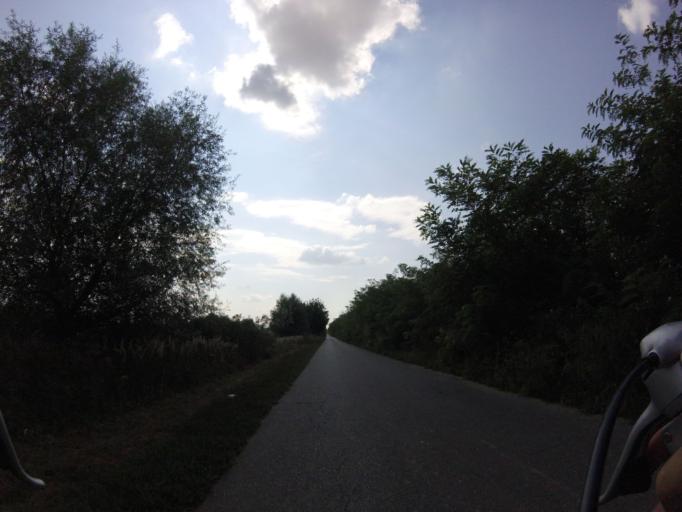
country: HU
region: Szabolcs-Szatmar-Bereg
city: Anarcs
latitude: 48.1660
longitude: 22.1827
